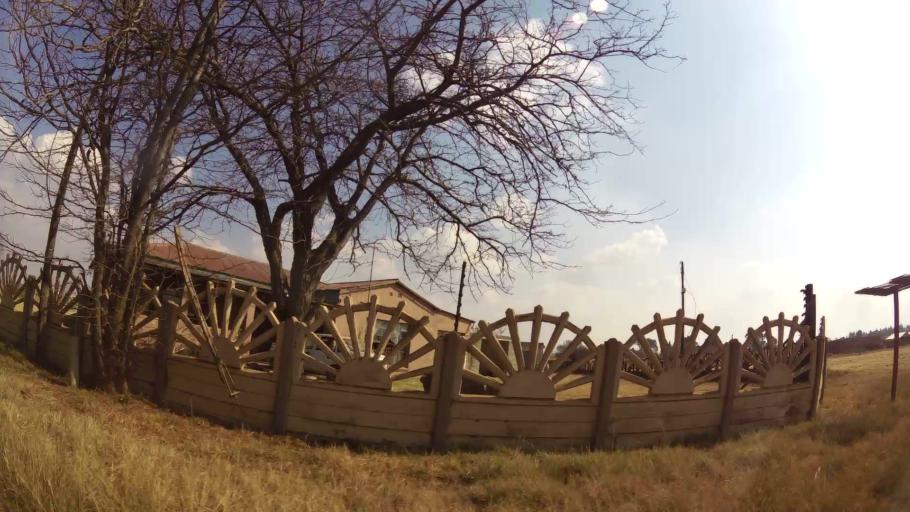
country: ZA
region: Gauteng
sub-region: Ekurhuleni Metropolitan Municipality
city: Springs
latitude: -26.1990
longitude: 28.5377
